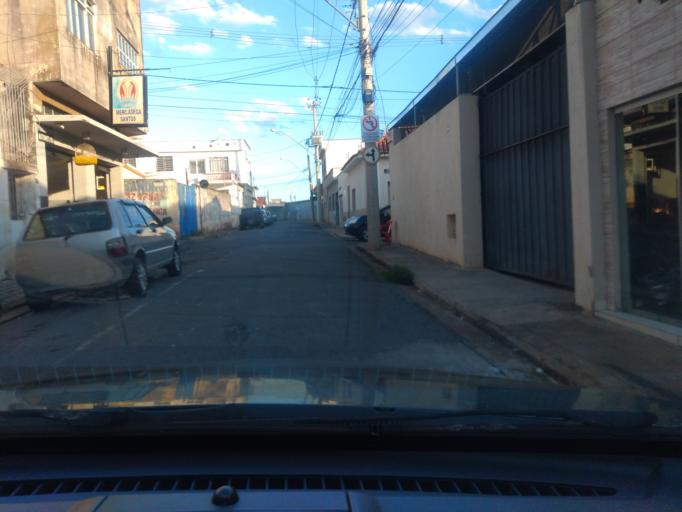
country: BR
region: Minas Gerais
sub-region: Tres Coracoes
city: Tres Coracoes
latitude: -21.6973
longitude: -45.2518
